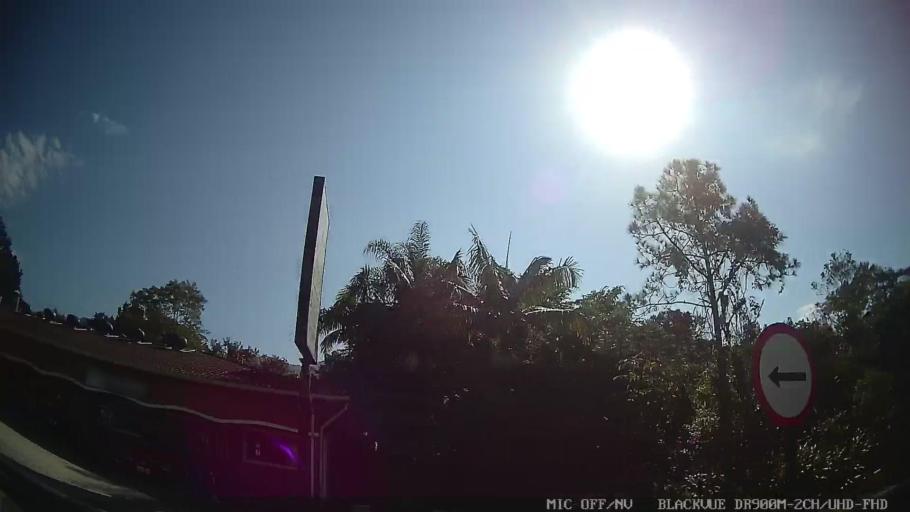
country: BR
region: Sao Paulo
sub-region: Bertioga
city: Bertioga
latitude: -23.8815
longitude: -46.1927
